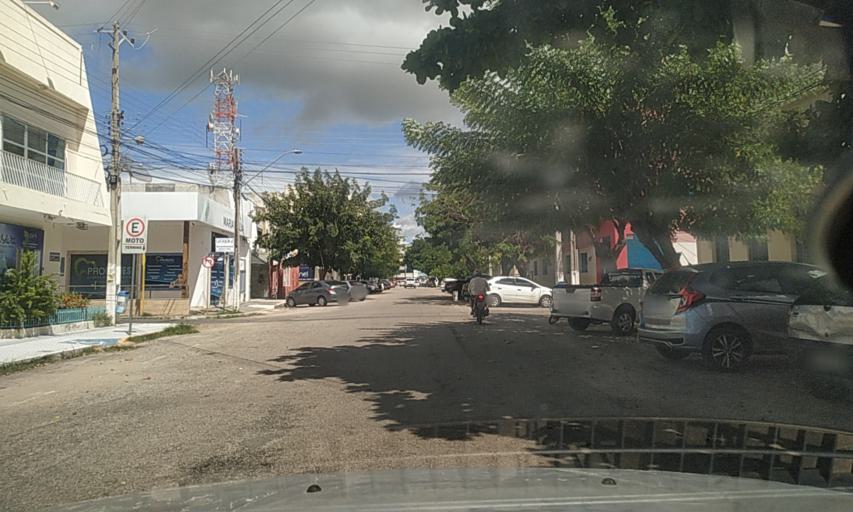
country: BR
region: Rio Grande do Norte
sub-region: Mossoro
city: Mossoro
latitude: -5.1909
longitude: -37.3396
